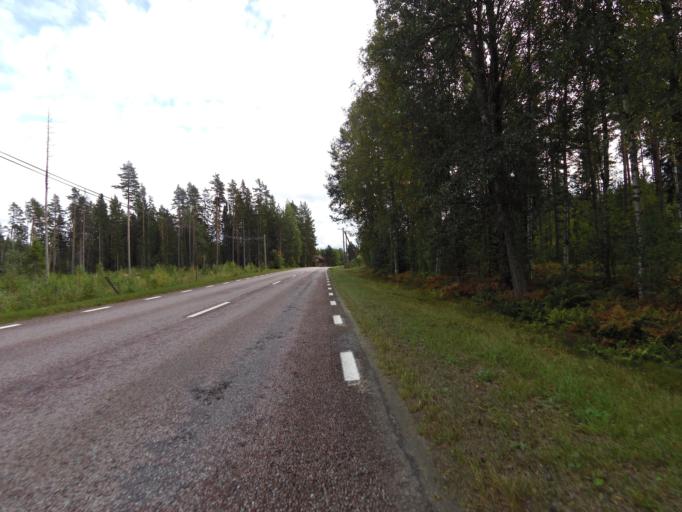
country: SE
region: Gaevleborg
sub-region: Sandvikens Kommun
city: Sandviken
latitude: 60.7129
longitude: 16.8057
